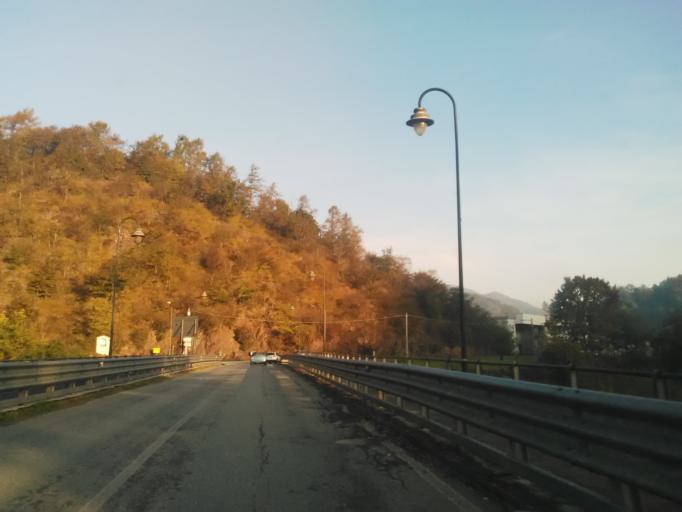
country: IT
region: Piedmont
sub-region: Provincia di Biella
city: Crevacuore
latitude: 45.6823
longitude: 8.2474
